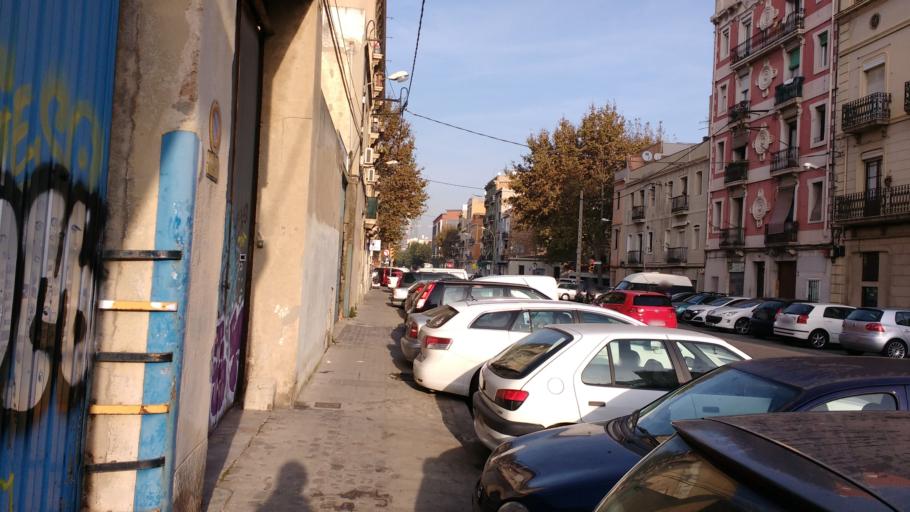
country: ES
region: Catalonia
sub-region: Provincia de Barcelona
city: Sant Marti
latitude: 41.3950
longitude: 2.2000
